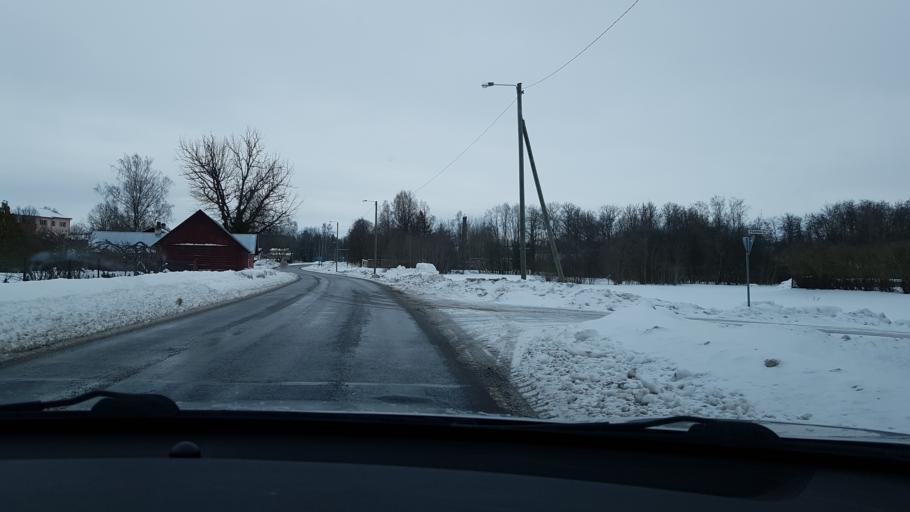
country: EE
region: Jaervamaa
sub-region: Jaerva-Jaani vald
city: Jarva-Jaani
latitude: 59.1475
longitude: 25.7522
